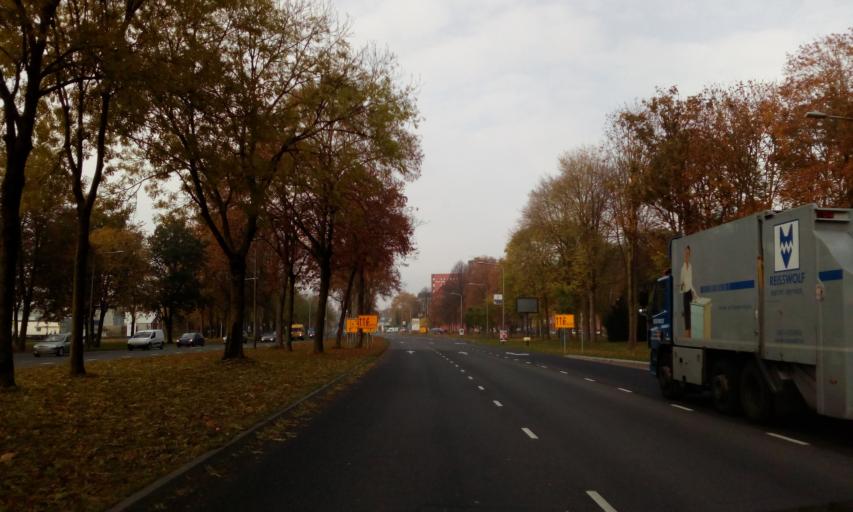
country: NL
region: Overijssel
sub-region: Gemeente Deventer
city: Deventer
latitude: 52.2395
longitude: 6.1766
